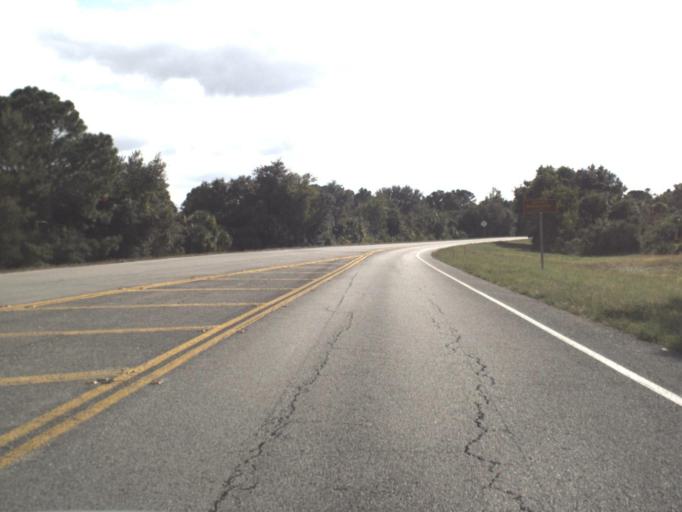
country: US
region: Florida
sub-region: Brevard County
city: Port Saint John
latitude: 28.5307
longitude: -80.8195
